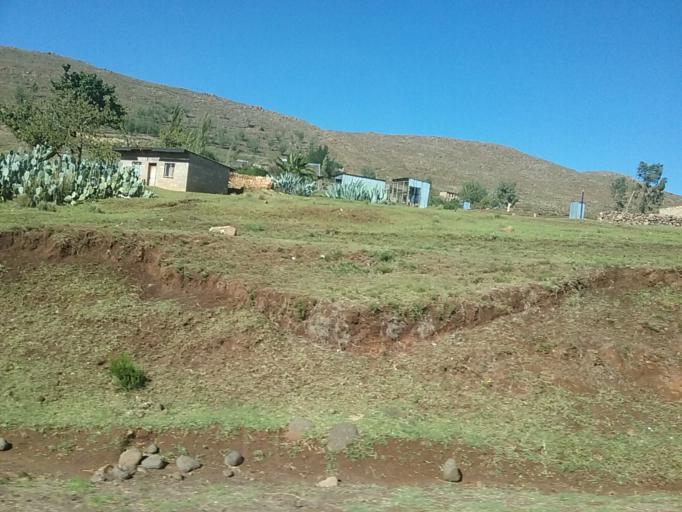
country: LS
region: Berea
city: Teyateyaneng
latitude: -29.2306
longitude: 27.8694
